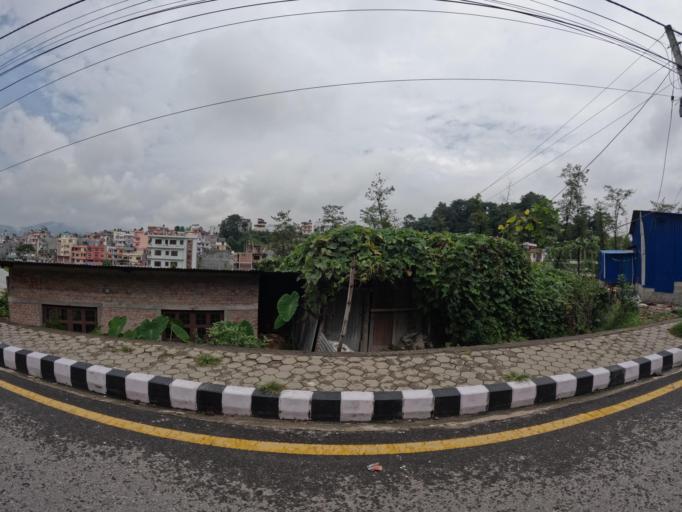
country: NP
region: Central Region
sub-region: Bagmati Zone
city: Kathmandu
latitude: 27.7583
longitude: 85.3255
